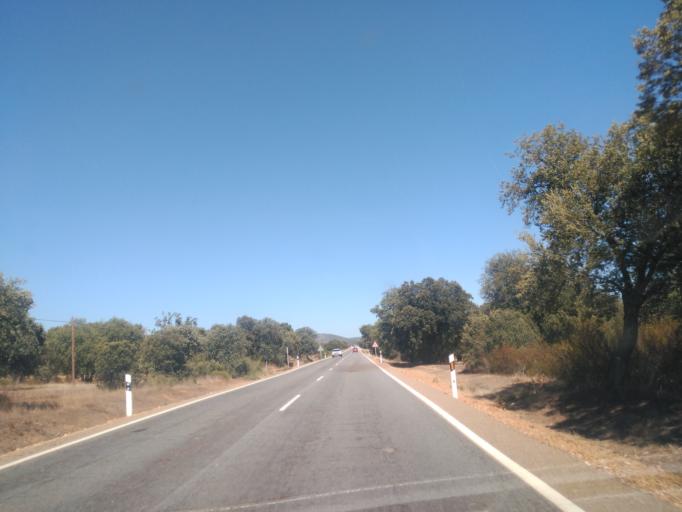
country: ES
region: Castille and Leon
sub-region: Provincia de Zamora
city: Tabara
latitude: 41.8104
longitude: -5.9339
